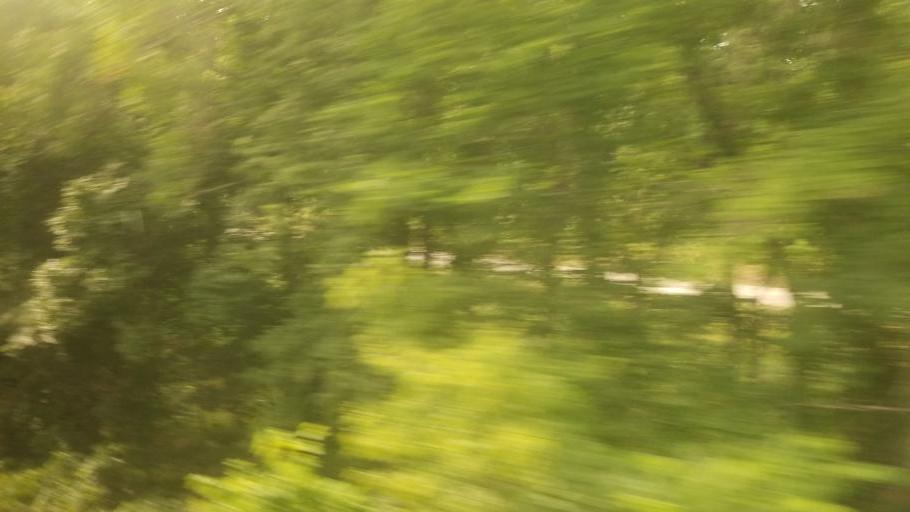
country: US
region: Kansas
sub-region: Douglas County
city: Lawrence
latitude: 39.0308
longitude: -95.3425
